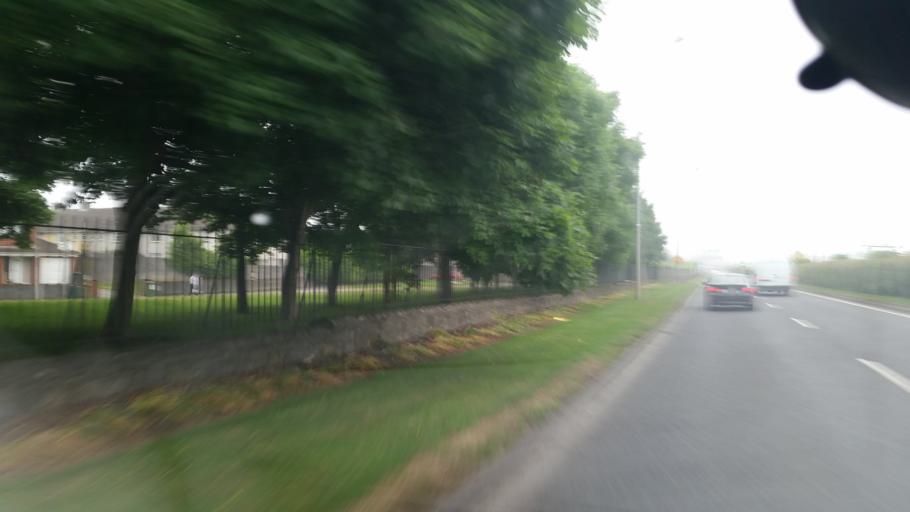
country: IE
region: Leinster
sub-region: Dublin City
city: Finglas
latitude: 53.3971
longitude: -6.3058
